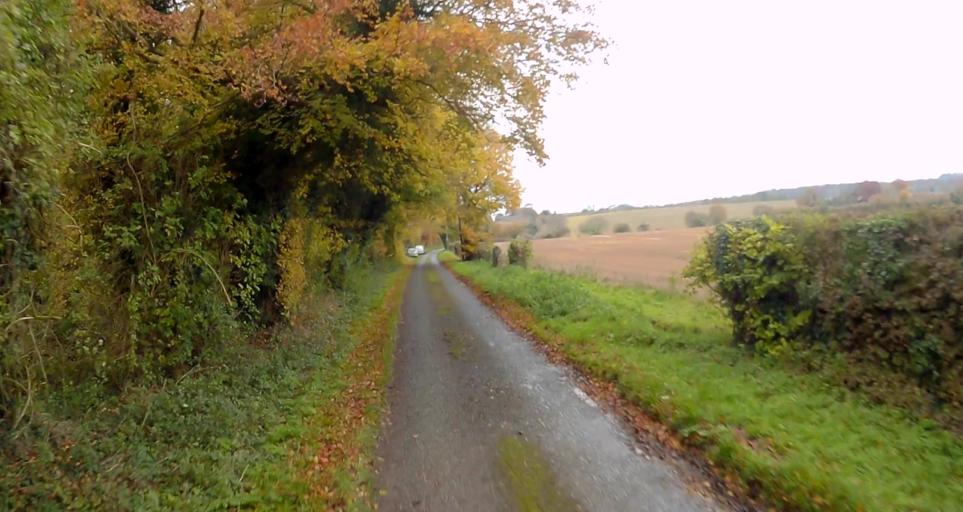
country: GB
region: England
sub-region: Hampshire
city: Long Sutton
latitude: 51.2389
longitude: -0.8865
